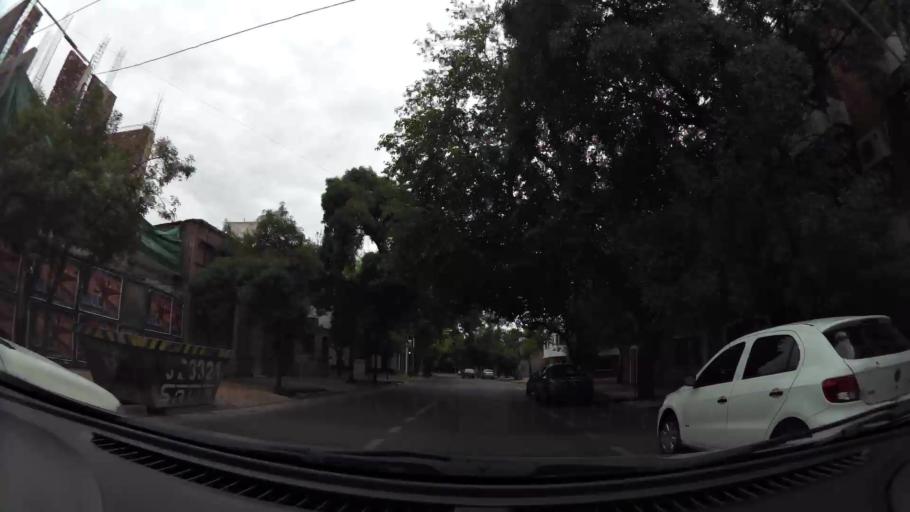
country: AR
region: Mendoza
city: Mendoza
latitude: -32.8952
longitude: -68.8591
